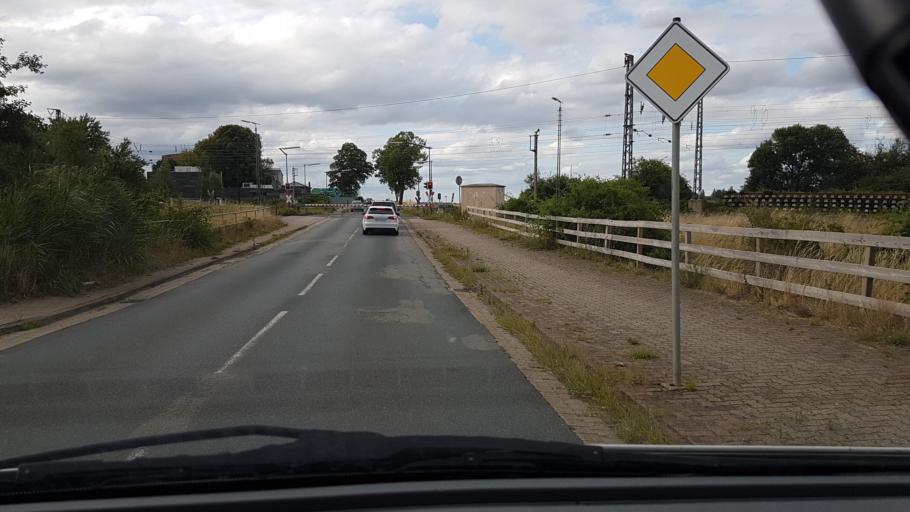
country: DE
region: Lower Saxony
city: Frellstedt
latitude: 52.2138
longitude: 10.9080
